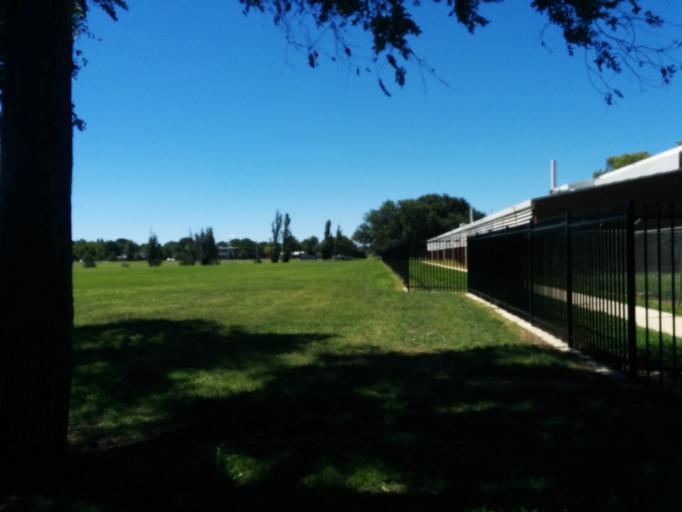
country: AU
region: Australian Capital Territory
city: Acton
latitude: -35.2532
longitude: 149.1292
